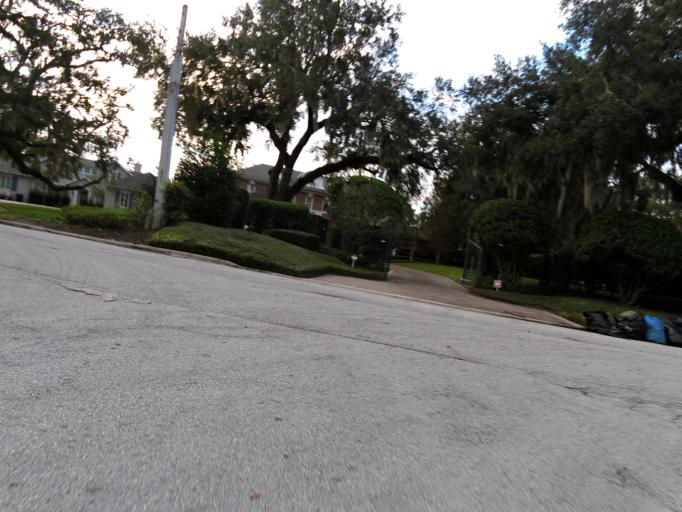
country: US
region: Florida
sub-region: Duval County
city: Jacksonville
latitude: 30.2813
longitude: -81.6628
